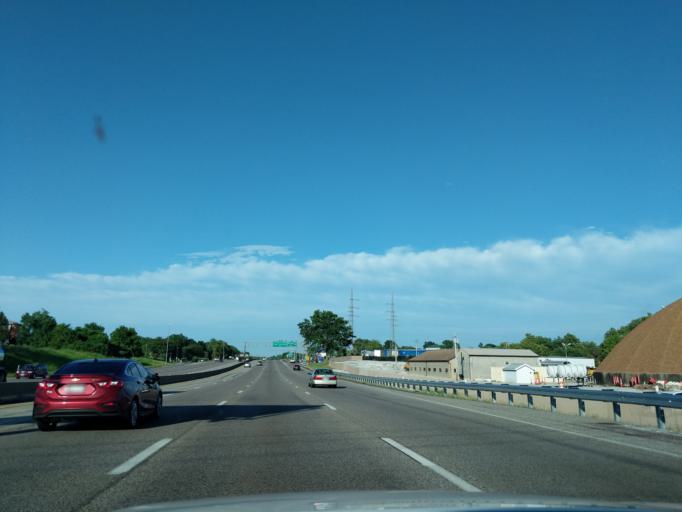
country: US
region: Missouri
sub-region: Saint Louis County
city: Lemay
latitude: 38.5448
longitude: -90.2947
